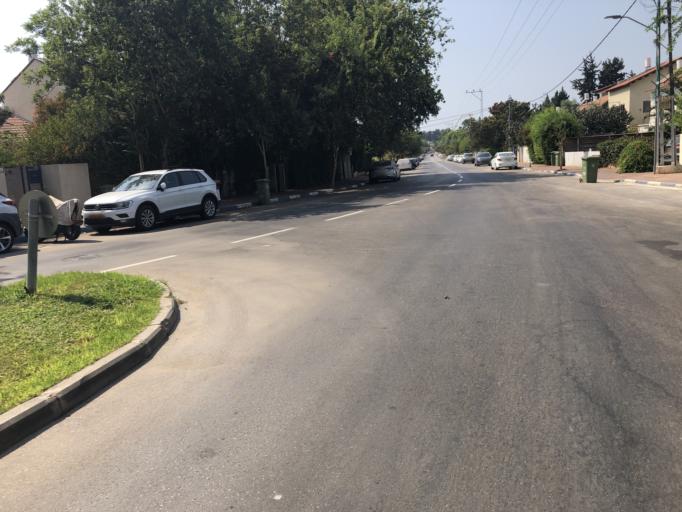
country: IL
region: Tel Aviv
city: Bene Beraq
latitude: 32.0564
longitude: 34.8323
